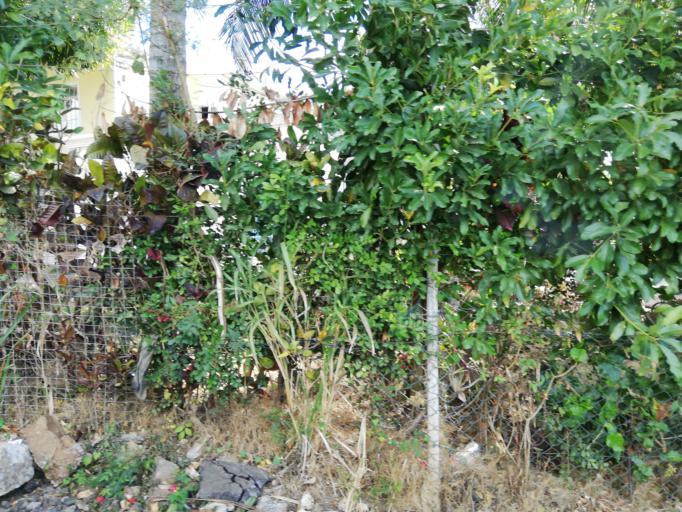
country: MU
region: Black River
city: Petite Riviere
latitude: -20.2219
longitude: 57.4566
